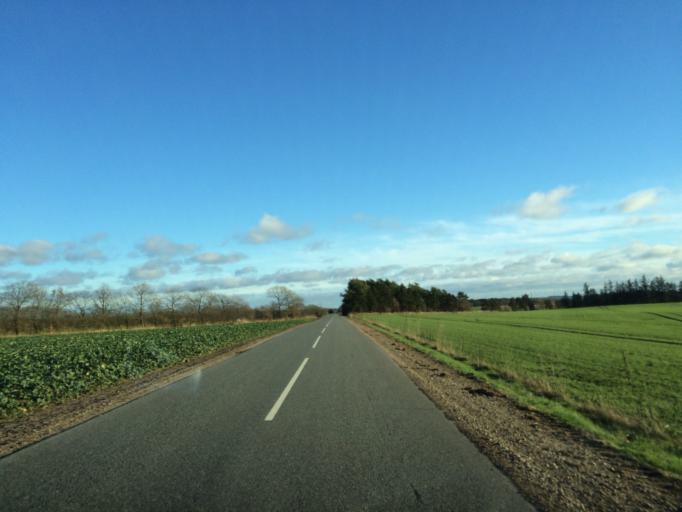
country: DK
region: Central Jutland
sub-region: Herning Kommune
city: Kibaek
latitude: 56.0432
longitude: 8.8217
